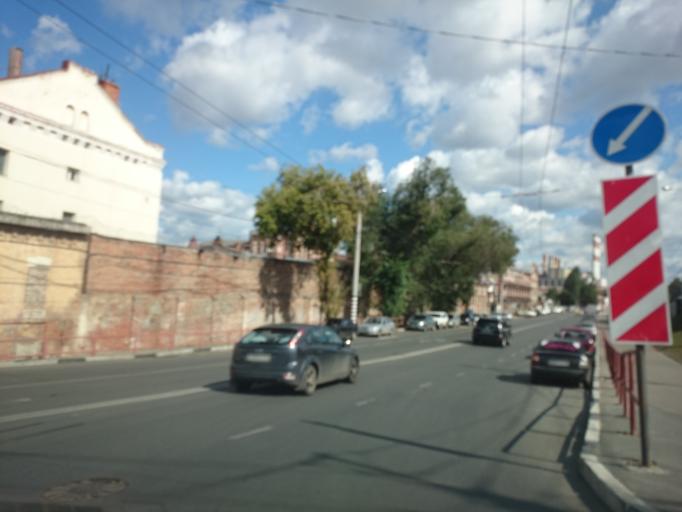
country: RU
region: Samara
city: Samara
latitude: 53.1993
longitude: 50.0970
